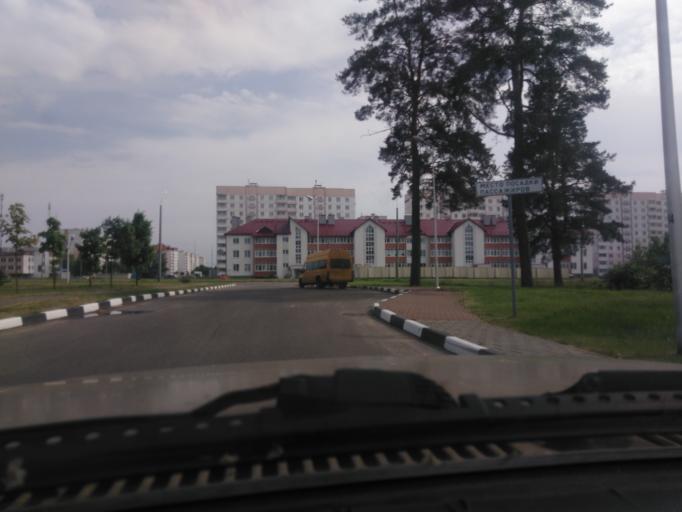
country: BY
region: Mogilev
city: Palykavichy Pyershyya
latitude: 53.9556
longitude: 30.3369
